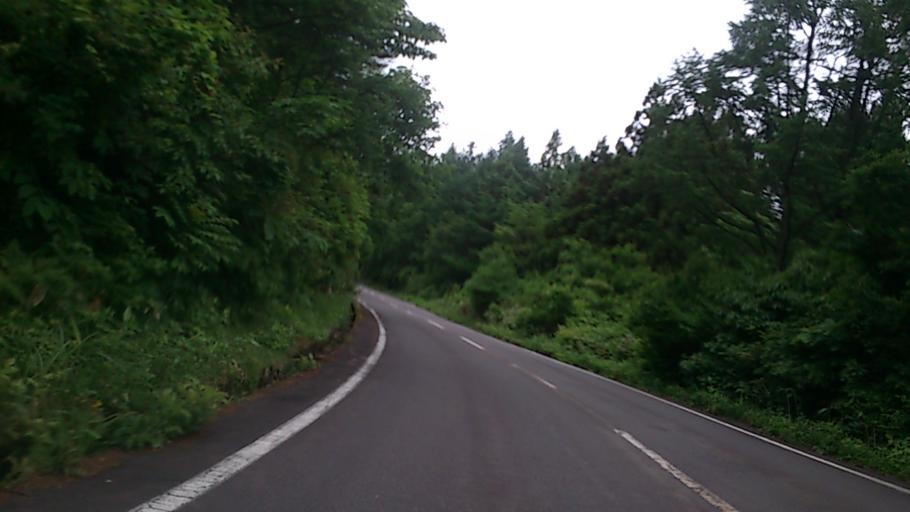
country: JP
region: Yamagata
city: Yuza
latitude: 39.1402
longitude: 139.9719
